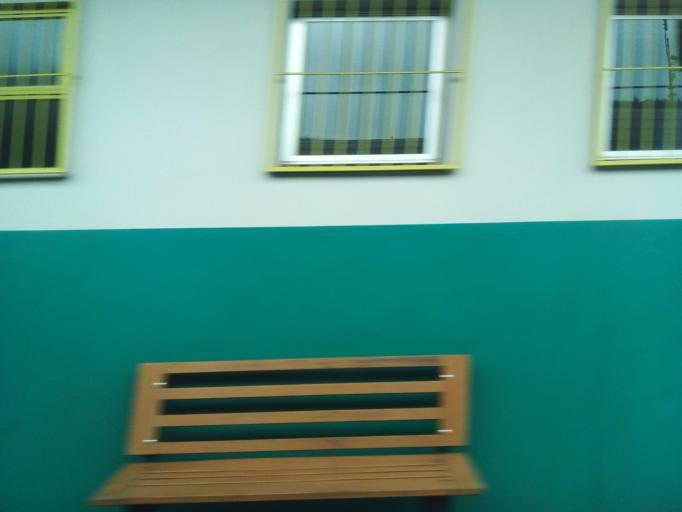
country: BR
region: Minas Gerais
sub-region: Rio Piracicaba
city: Rio Piracicaba
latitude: -19.9318
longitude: -43.1728
